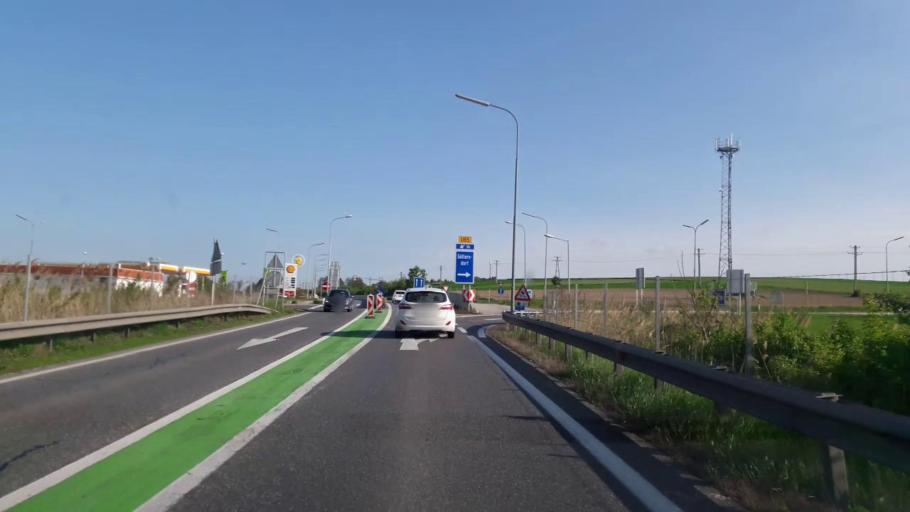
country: AT
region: Lower Austria
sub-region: Politischer Bezirk Hollabrunn
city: Gollersdorf
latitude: 48.4933
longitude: 16.1081
